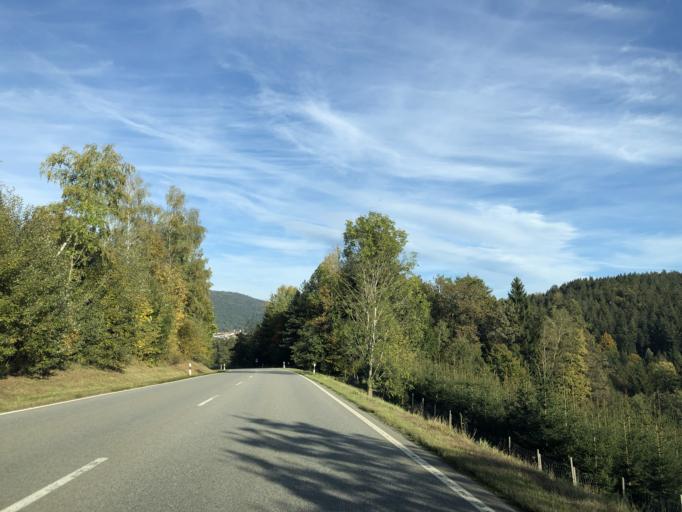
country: DE
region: Bavaria
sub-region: Lower Bavaria
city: Bobrach
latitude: 49.0608
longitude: 13.0646
